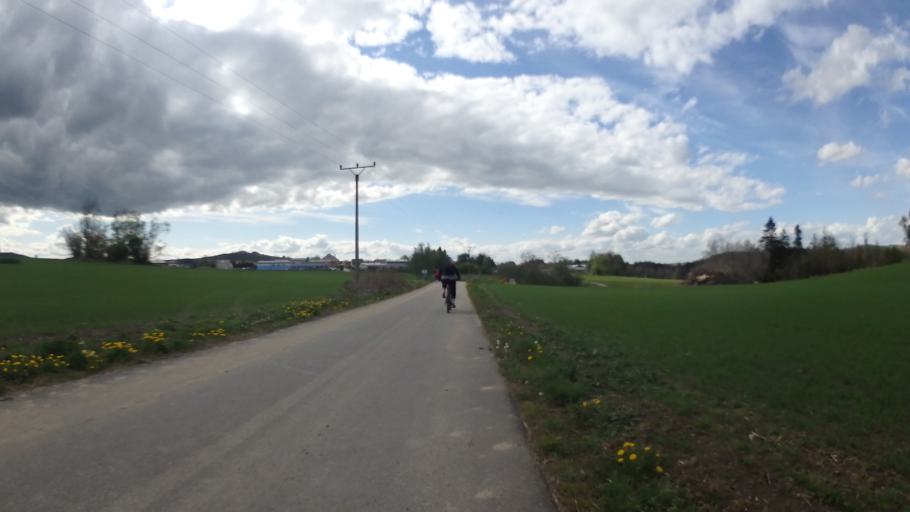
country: CZ
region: Vysocina
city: Merin
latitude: 49.3608
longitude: 15.9125
